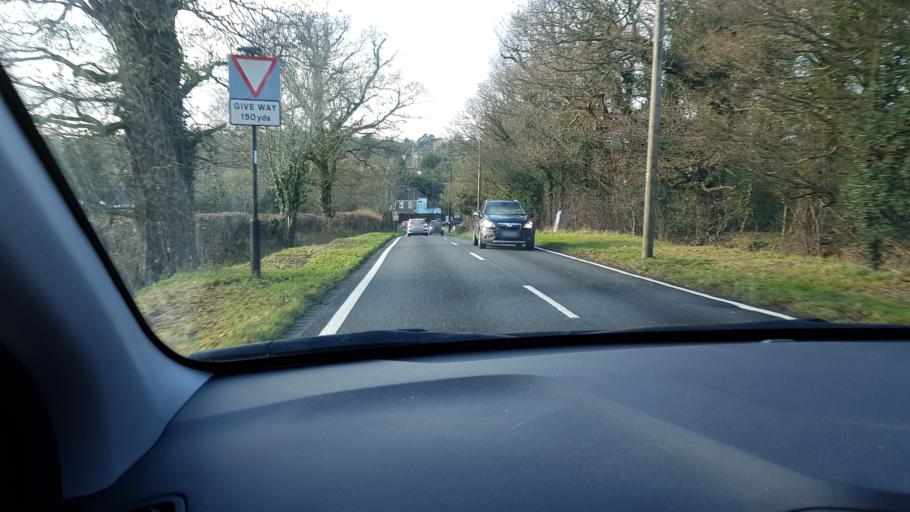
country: GB
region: England
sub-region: Greater London
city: Hadley Wood
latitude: 51.6669
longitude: -0.1551
